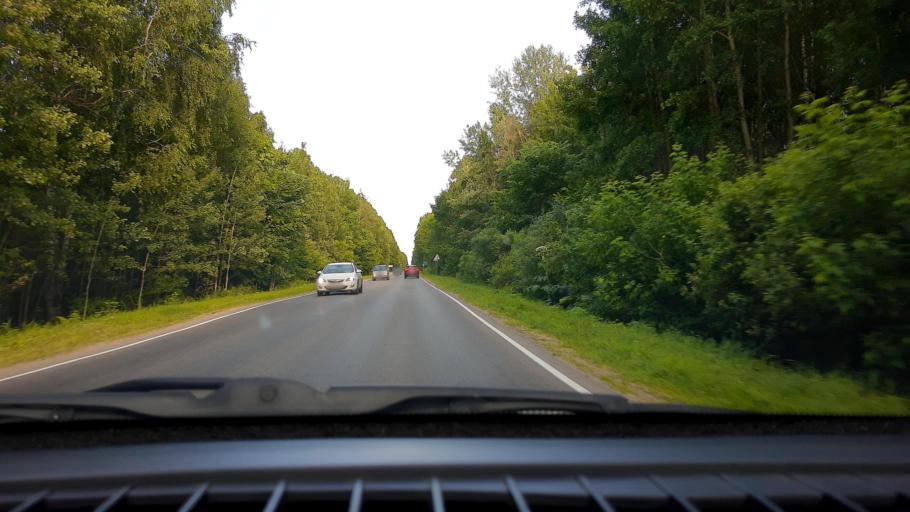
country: RU
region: Nizjnij Novgorod
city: Afonino
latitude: 56.3033
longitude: 44.2536
